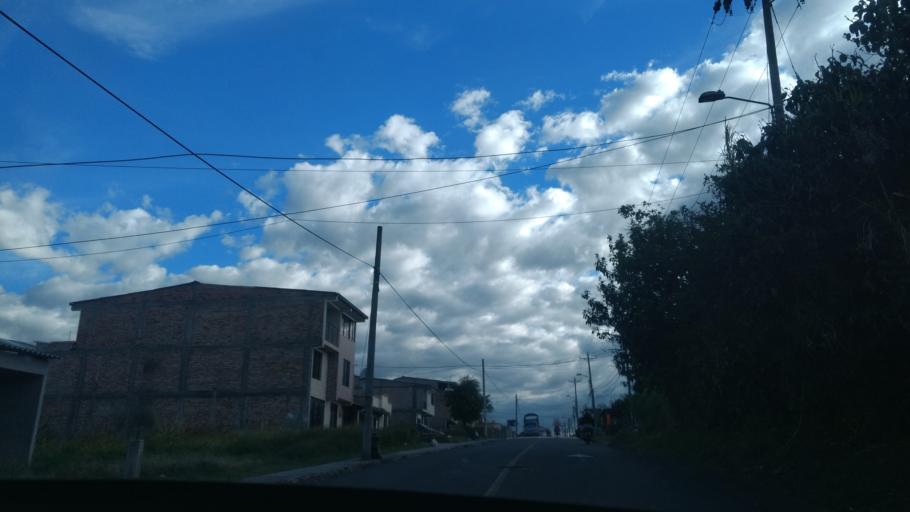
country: CO
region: Cauca
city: Popayan
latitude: 2.4851
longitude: -76.5773
